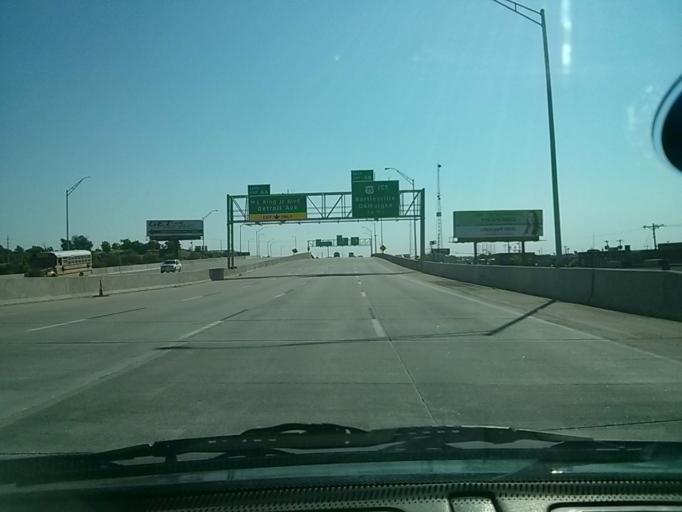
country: US
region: Oklahoma
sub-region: Tulsa County
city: Tulsa
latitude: 36.1608
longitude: -95.9978
